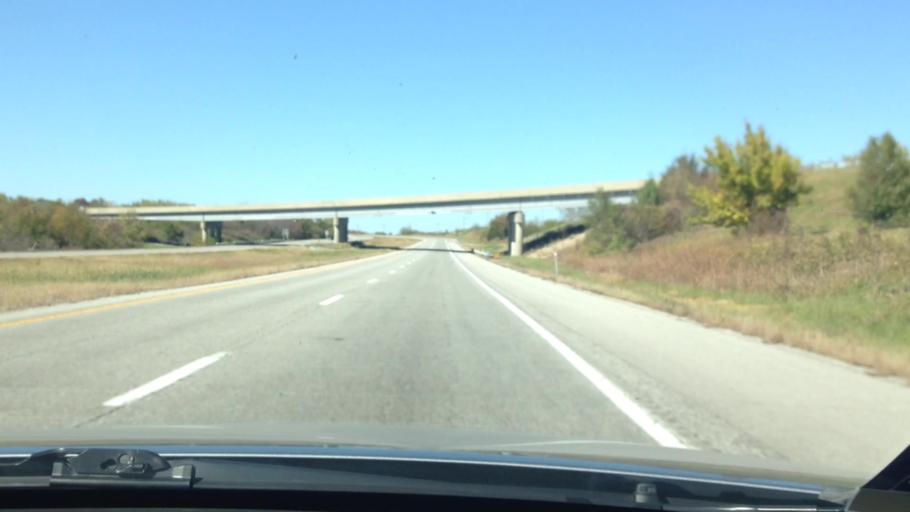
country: US
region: Missouri
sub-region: Platte County
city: Weatherby Lake
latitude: 39.3111
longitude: -94.6722
